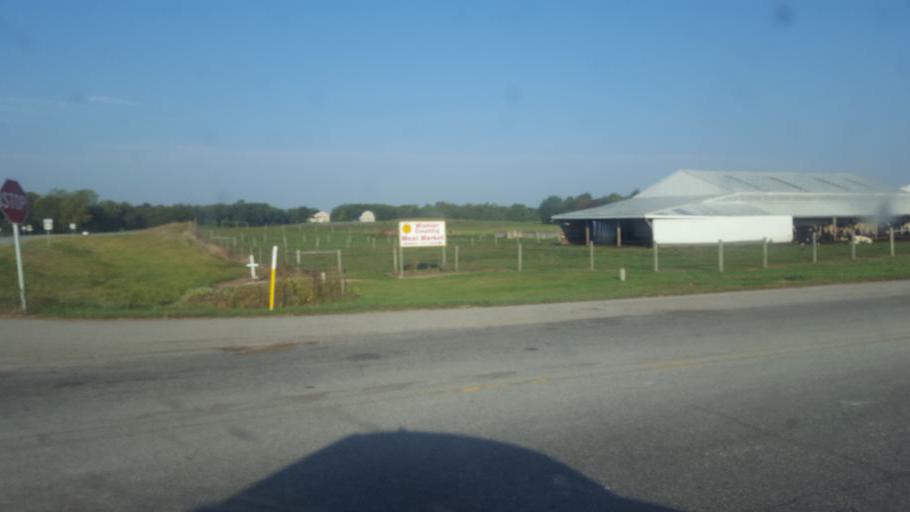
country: US
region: Indiana
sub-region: LaGrange County
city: Topeka
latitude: 41.6406
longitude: -85.5412
